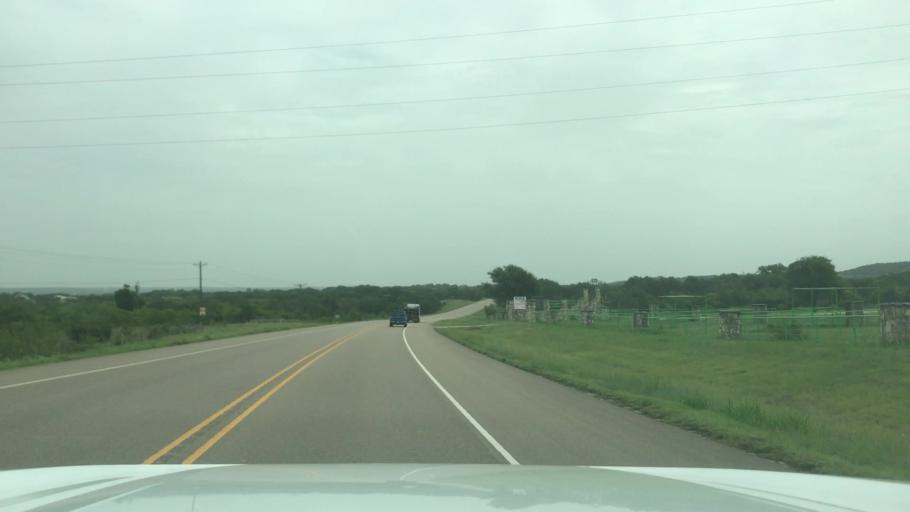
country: US
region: Texas
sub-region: Bosque County
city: Meridian
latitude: 31.9439
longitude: -97.7176
